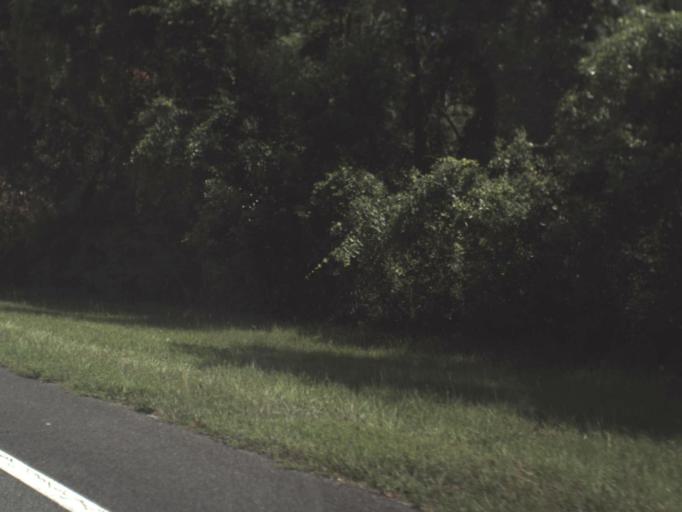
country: US
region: Florida
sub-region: Levy County
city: Manatee Road
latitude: 29.5722
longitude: -82.9133
